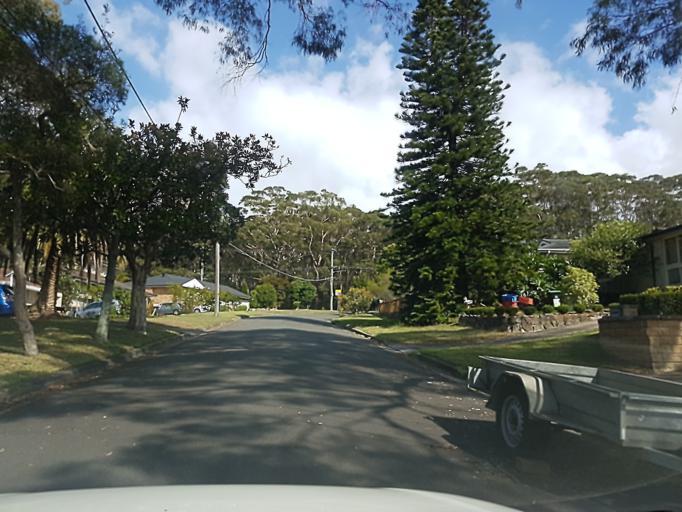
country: AU
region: New South Wales
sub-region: Warringah
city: Davidson
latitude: -33.7457
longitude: 151.2078
